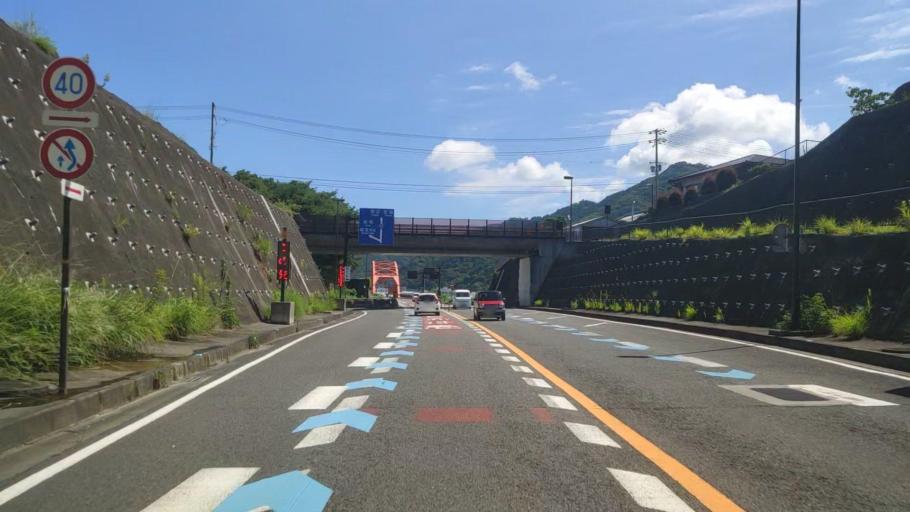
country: JP
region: Wakayama
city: Shingu
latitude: 33.7364
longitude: 135.9885
